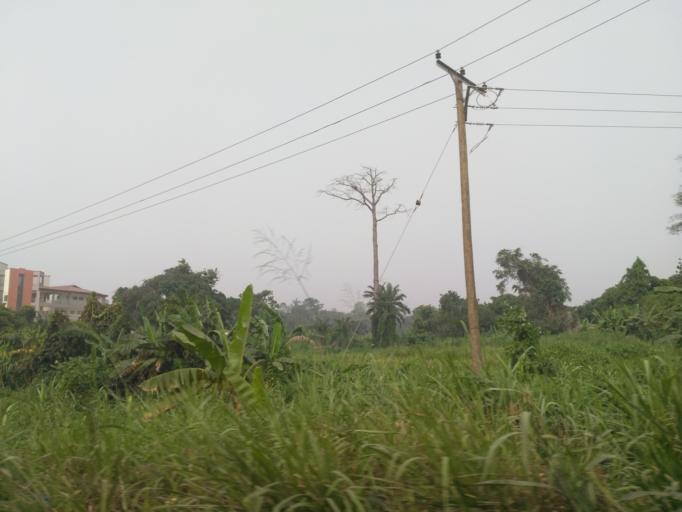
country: GH
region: Ashanti
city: Kumasi
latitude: 6.6884
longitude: -1.6272
